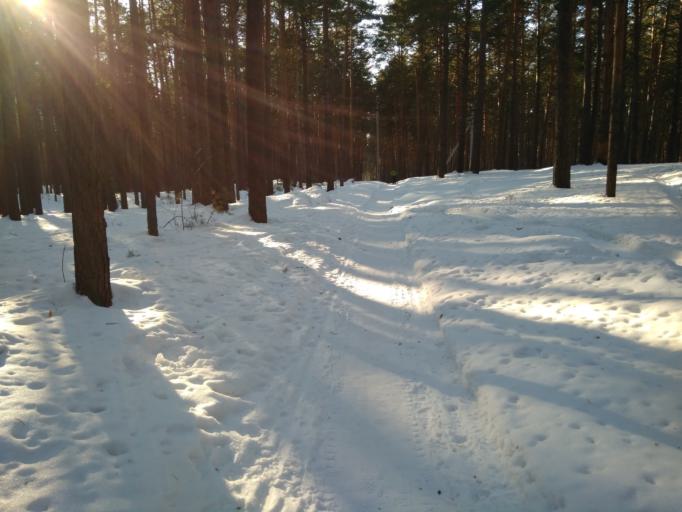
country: RU
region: Tomsk
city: Timiryazevskoye
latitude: 56.4857
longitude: 84.8797
